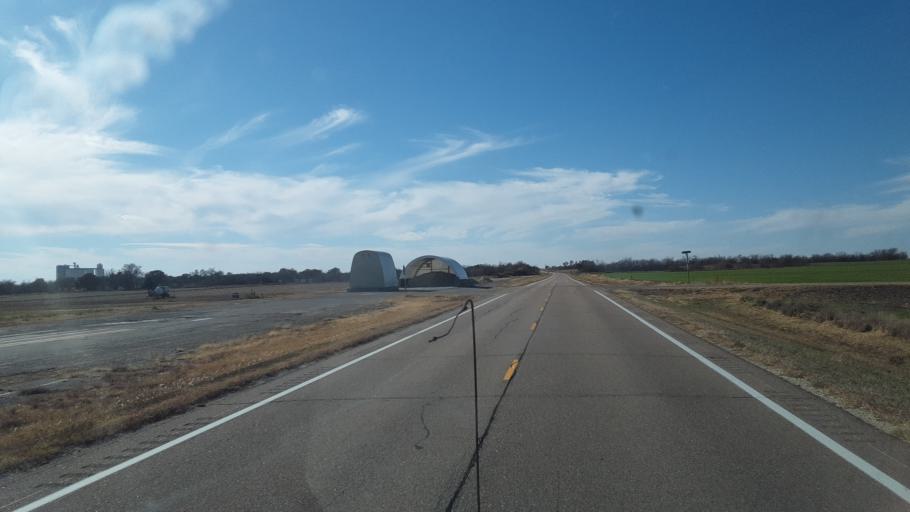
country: US
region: Kansas
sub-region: Pawnee County
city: Larned
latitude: 38.1896
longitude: -99.2949
